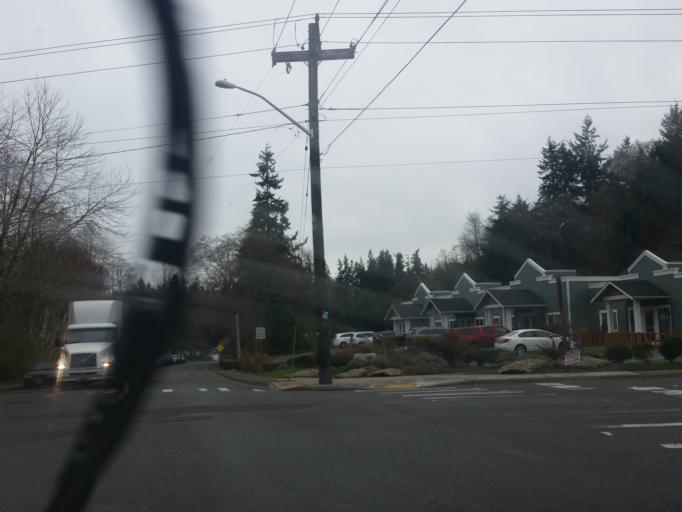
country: US
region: Washington
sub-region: Snohomish County
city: Meadowdale
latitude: 47.8314
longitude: -122.3376
